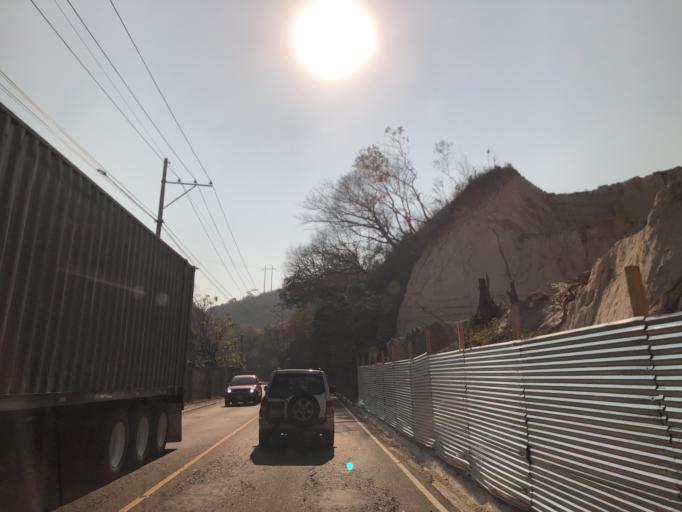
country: GT
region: Guatemala
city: Petapa
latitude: 14.5039
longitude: -90.5420
